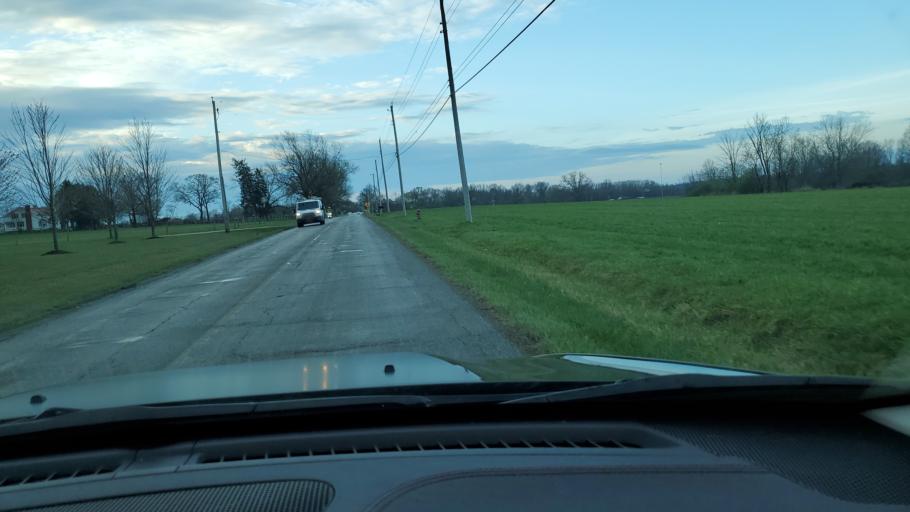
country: US
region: Ohio
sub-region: Trumbull County
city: Mineral Ridge
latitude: 41.1375
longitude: -80.7398
